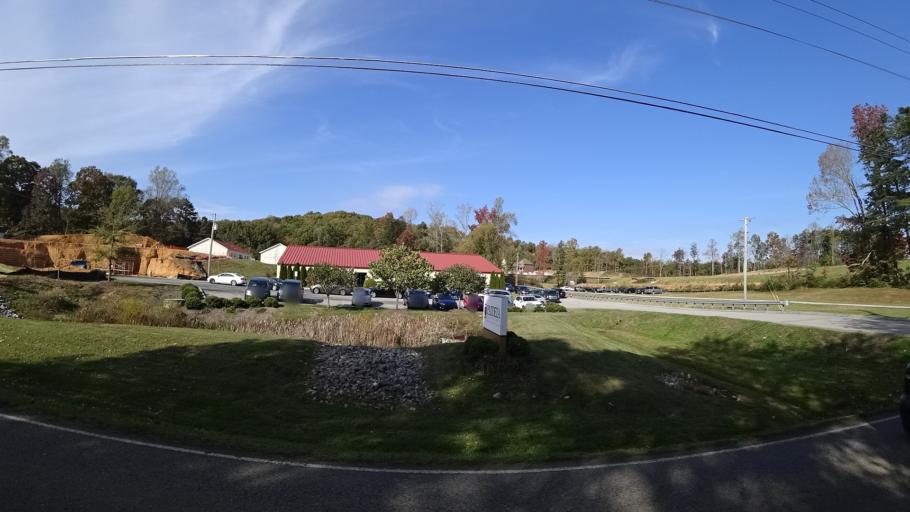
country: US
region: Tennessee
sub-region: Knox County
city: Farragut
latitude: 35.9319
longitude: -84.1548
